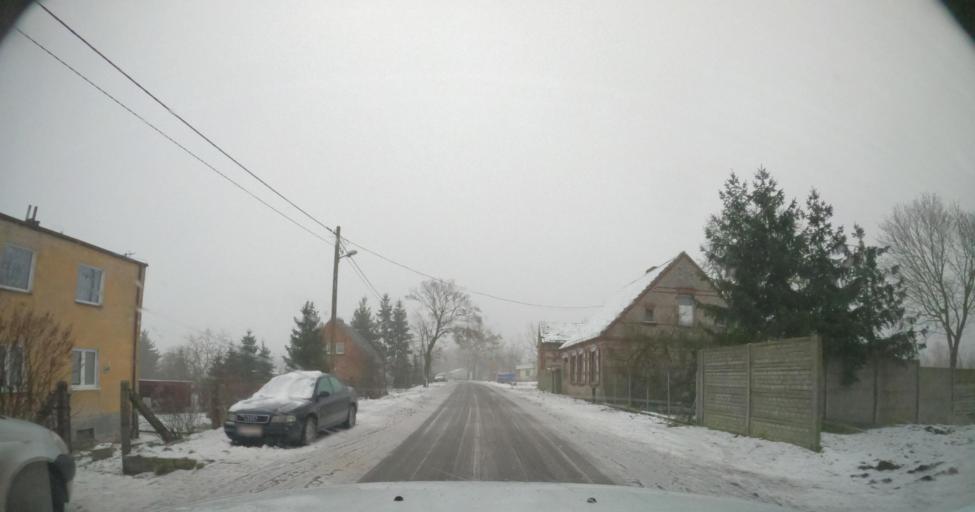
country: PL
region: West Pomeranian Voivodeship
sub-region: Powiat policki
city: Police
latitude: 53.5573
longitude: 14.6286
